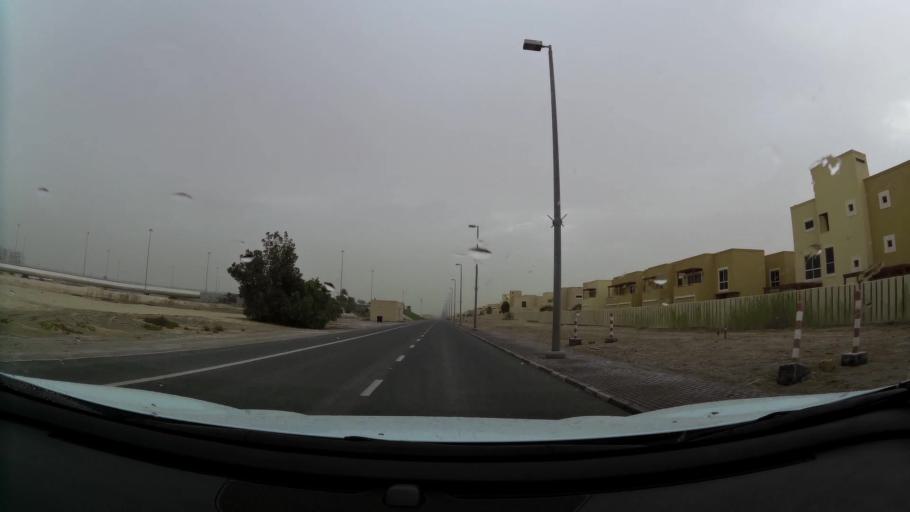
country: AE
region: Abu Dhabi
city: Abu Dhabi
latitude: 24.4379
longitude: 54.5830
